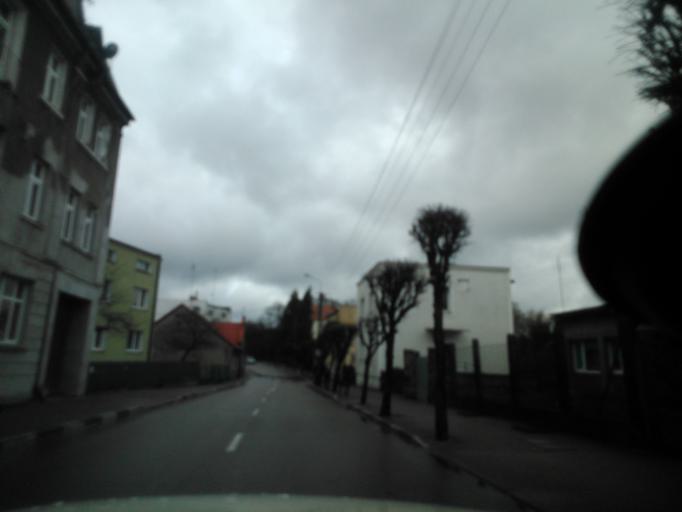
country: PL
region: Warmian-Masurian Voivodeship
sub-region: Powiat dzialdowski
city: Lidzbark
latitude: 53.2647
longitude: 19.8210
